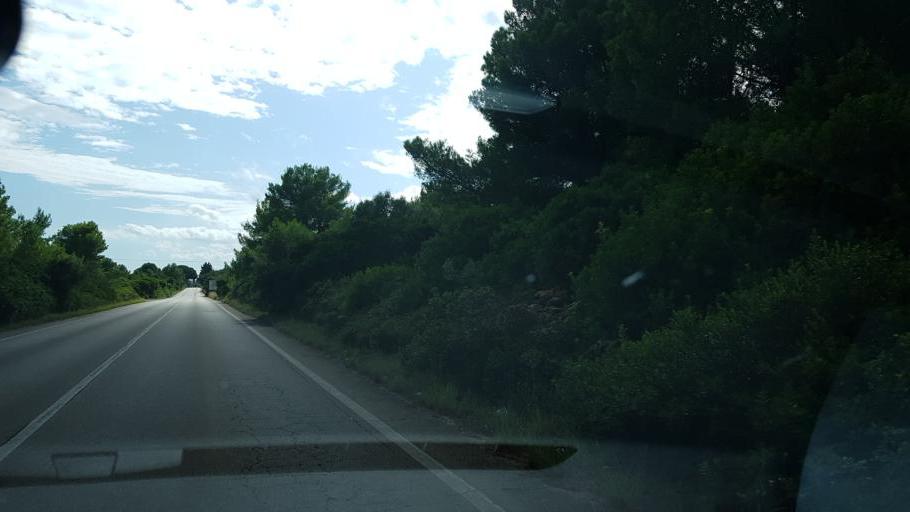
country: IT
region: Apulia
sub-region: Provincia di Lecce
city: Borgagne
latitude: 40.2389
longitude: 18.4443
